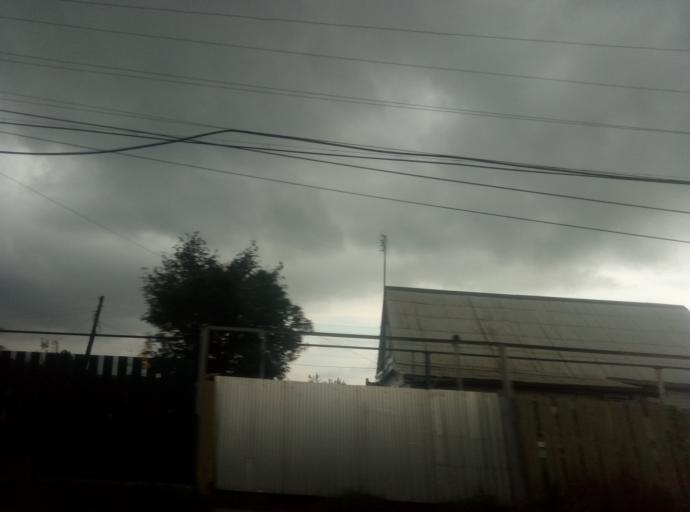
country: RU
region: Tula
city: Kireyevsk
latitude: 53.9765
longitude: 37.9311
